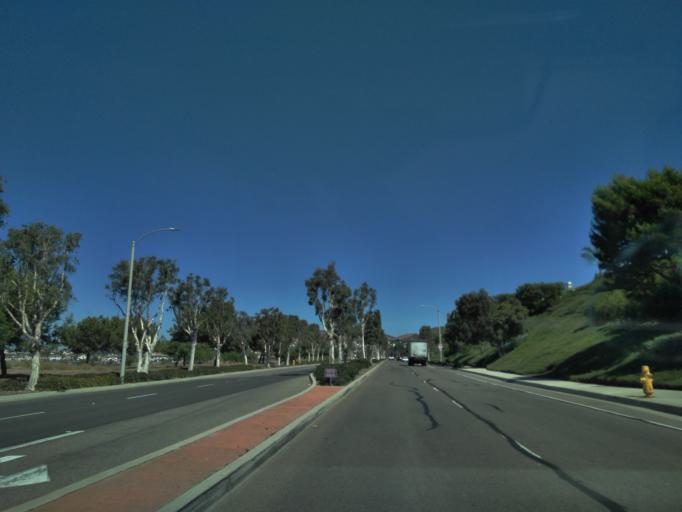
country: US
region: California
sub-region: Orange County
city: San Clemente
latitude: 33.4528
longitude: -117.6214
